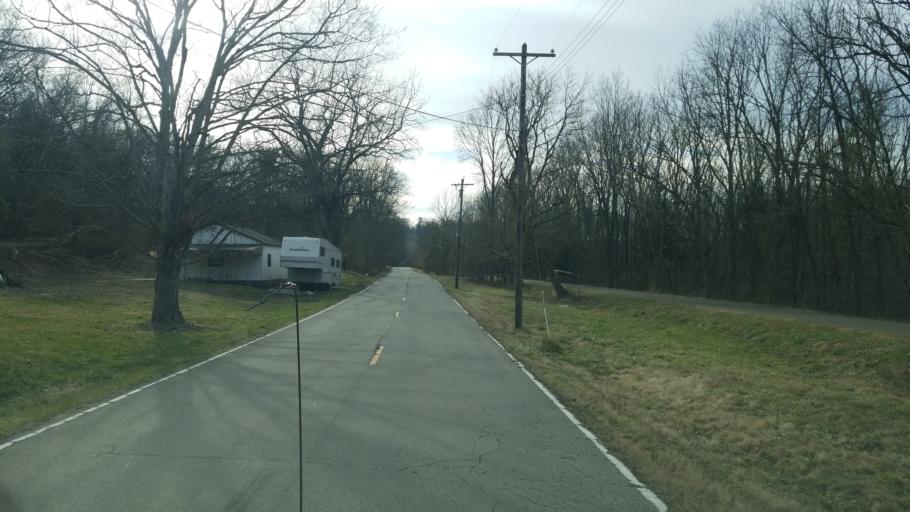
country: US
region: Ohio
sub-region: Warren County
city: Morrow
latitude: 39.4403
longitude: -84.1010
